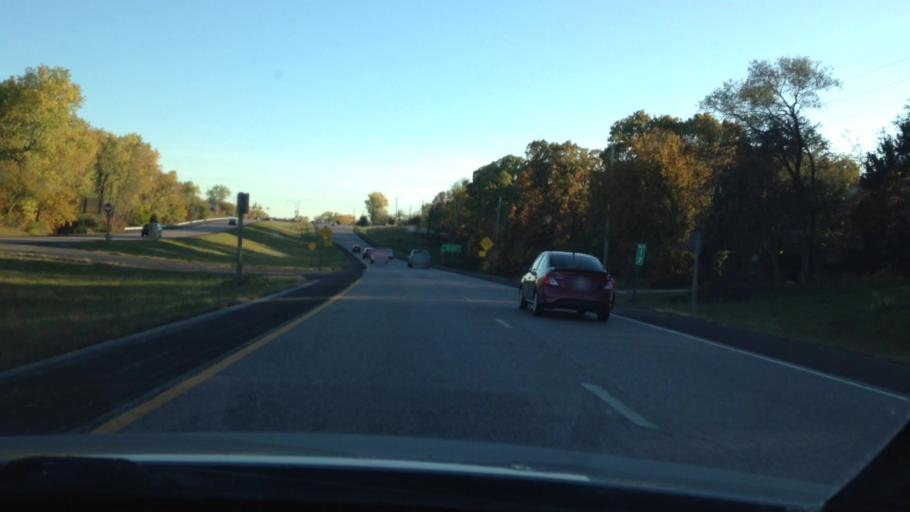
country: US
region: Kansas
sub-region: Leavenworth County
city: Basehor
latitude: 39.1333
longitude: -94.9011
